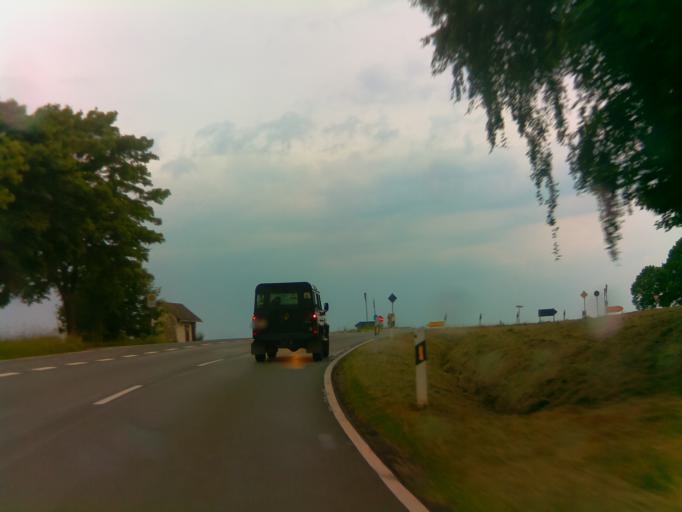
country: DE
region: Lower Saxony
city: Heyen
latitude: 52.0604
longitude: 9.5251
